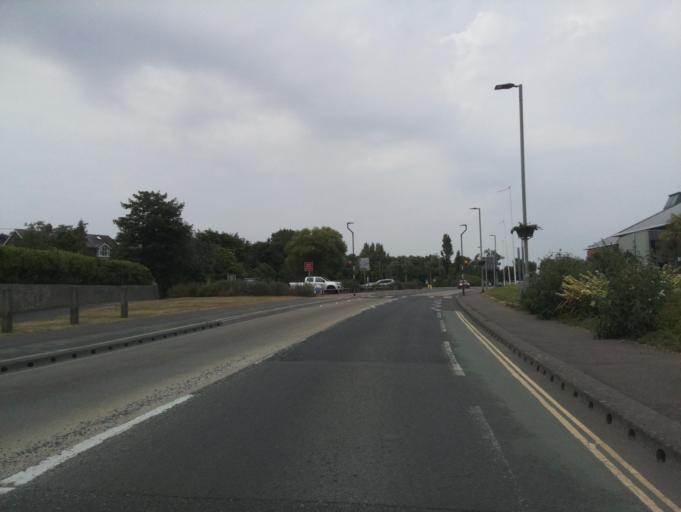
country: GB
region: England
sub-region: Devon
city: Colyton
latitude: 50.7056
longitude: -3.0682
